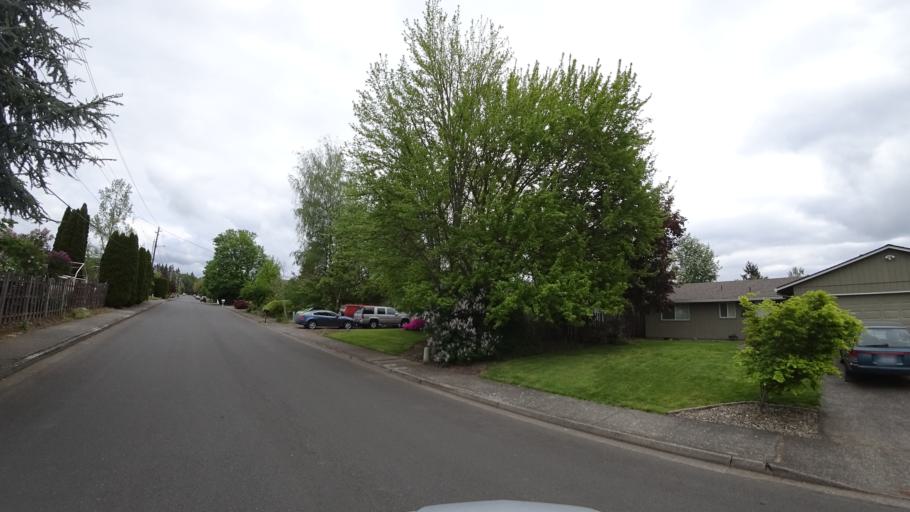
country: US
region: Oregon
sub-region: Washington County
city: Hillsboro
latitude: 45.5389
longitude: -122.9755
